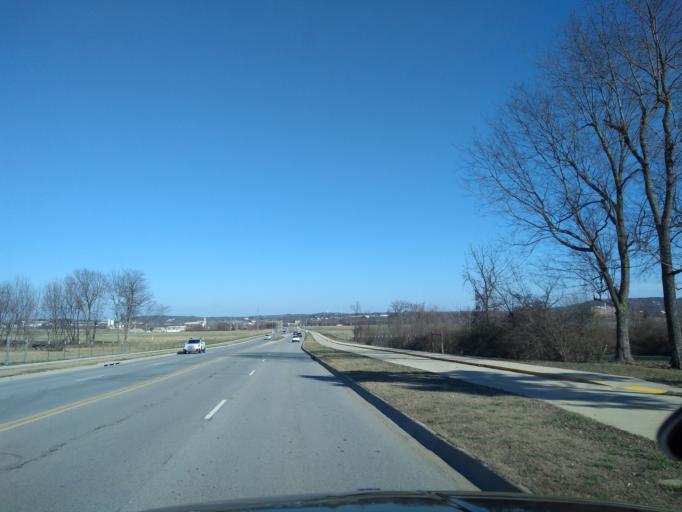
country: US
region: Arkansas
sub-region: Washington County
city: Johnson
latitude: 36.1173
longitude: -94.1754
